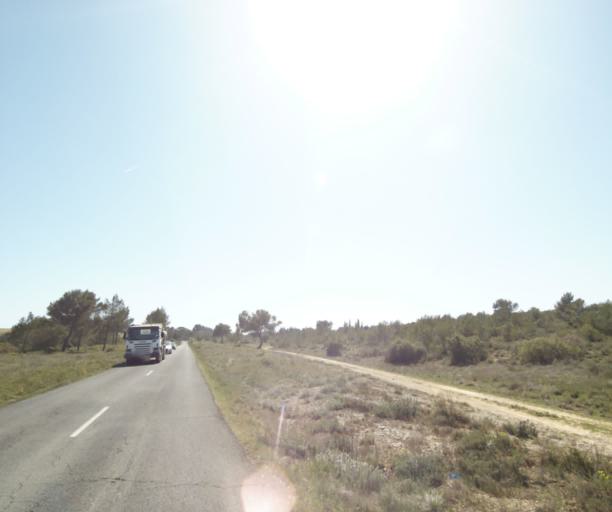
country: FR
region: Languedoc-Roussillon
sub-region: Departement de l'Herault
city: Saint-Drezery
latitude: 43.7273
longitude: 3.9554
